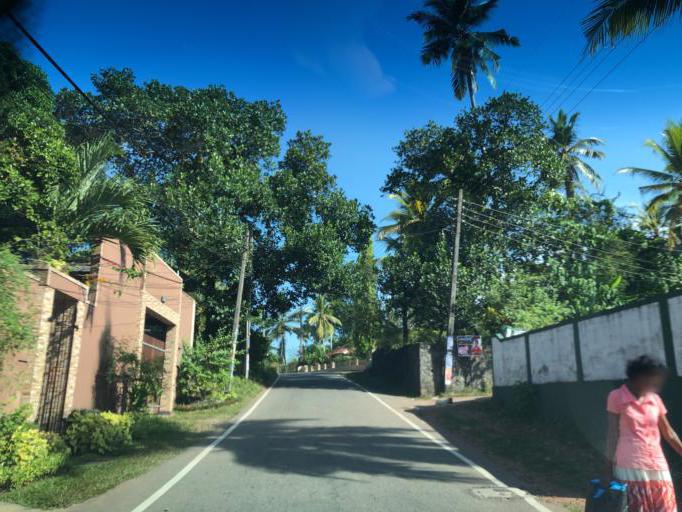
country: LK
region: Western
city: Homagama
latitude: 6.7905
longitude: 79.9791
